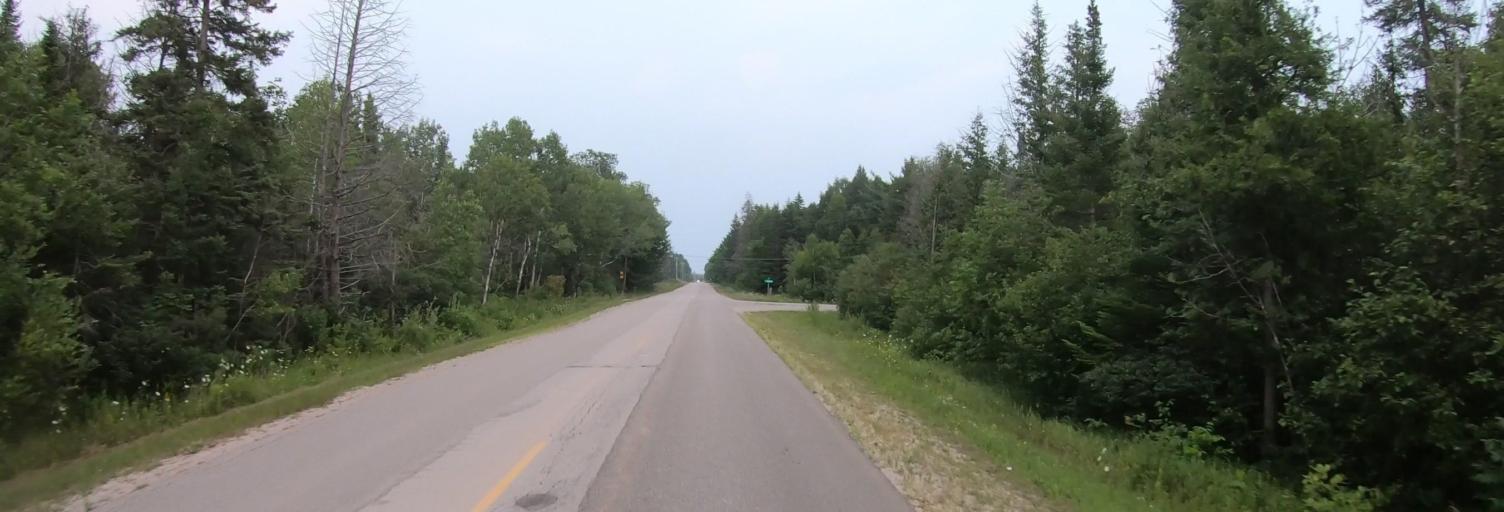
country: US
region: Michigan
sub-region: Mackinac County
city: Saint Ignace
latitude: 45.6945
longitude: -84.7930
